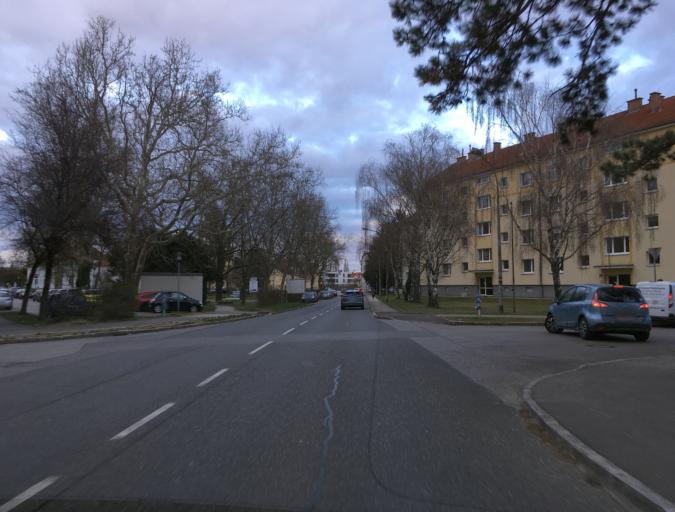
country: AT
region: Lower Austria
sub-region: Politischer Bezirk Korneuburg
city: Korneuburg
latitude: 48.3408
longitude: 16.3375
